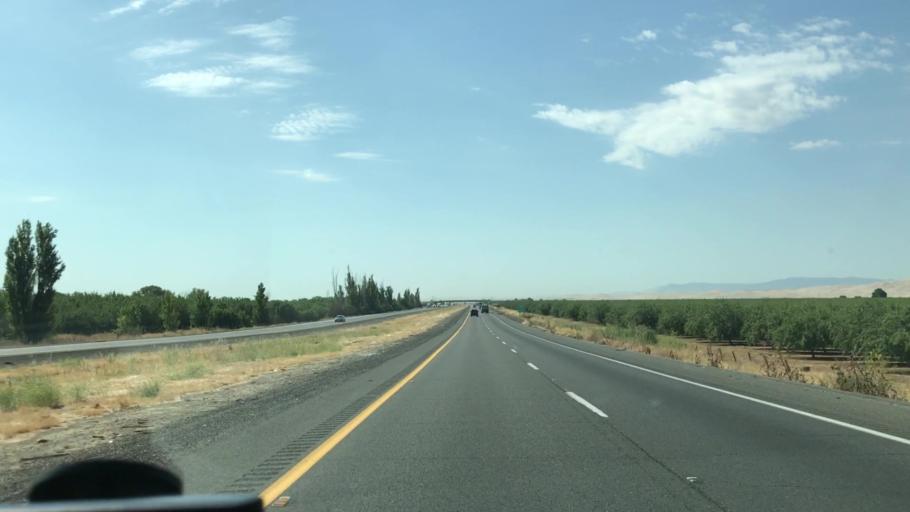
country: US
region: California
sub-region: Merced County
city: Gustine
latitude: 37.1430
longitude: -121.0410
